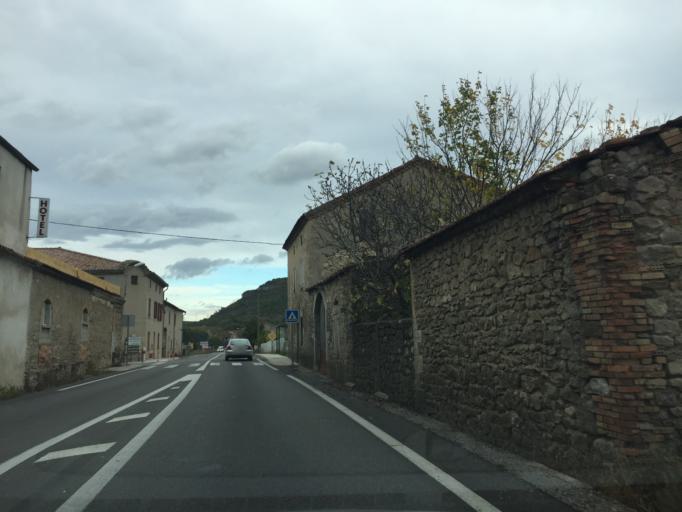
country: FR
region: Rhone-Alpes
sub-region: Departement de l'Ardeche
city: Largentiere
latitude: 44.5051
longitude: 4.3100
